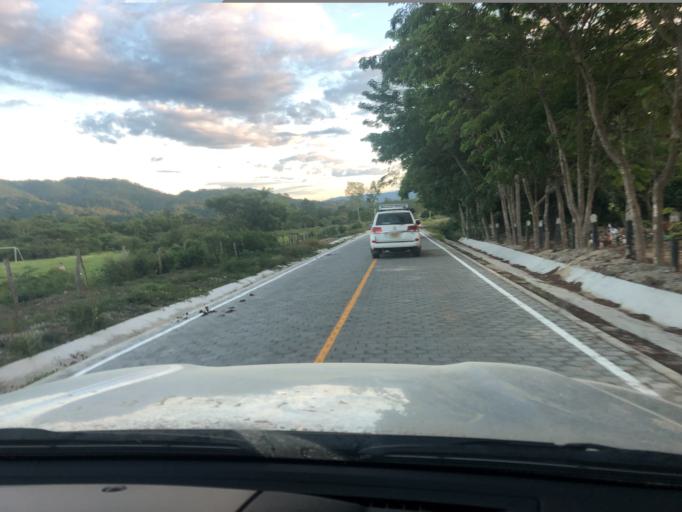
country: HN
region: El Paraiso
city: Santa Cruz
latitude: 13.7240
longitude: -86.6226
